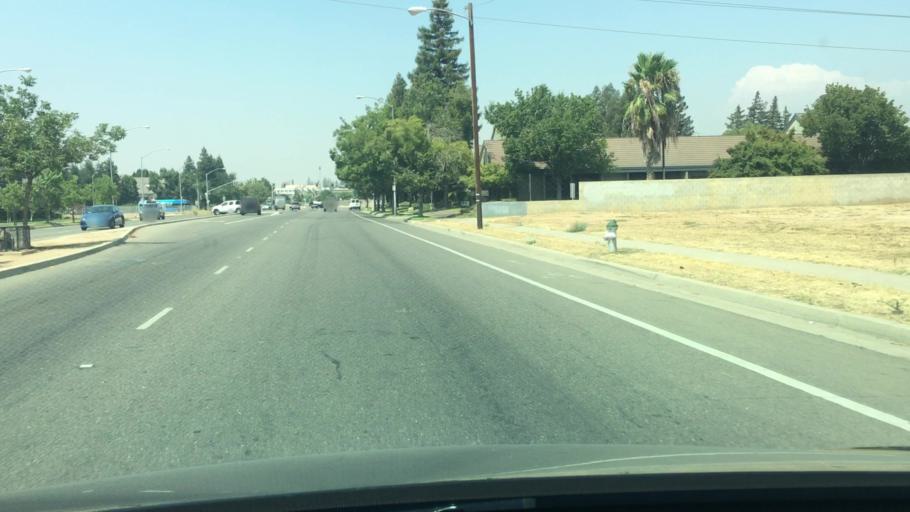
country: US
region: California
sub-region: Fresno County
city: Clovis
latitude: 36.8497
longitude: -119.7837
